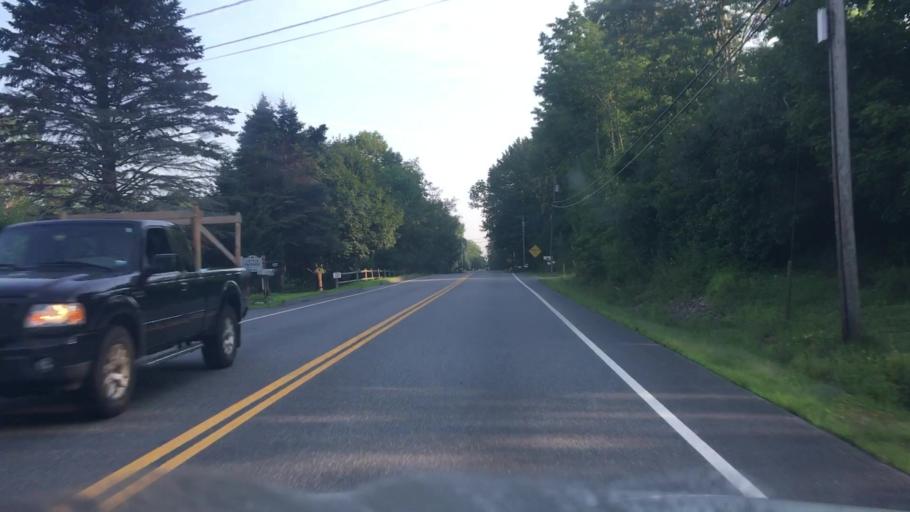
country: US
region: Maine
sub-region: Cumberland County
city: Freeport
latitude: 43.9147
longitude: -70.0905
